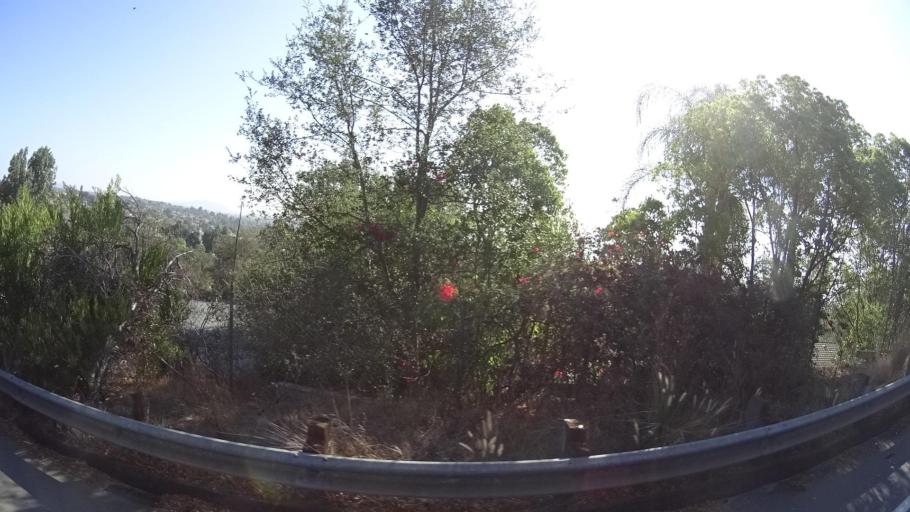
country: US
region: California
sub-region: San Diego County
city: Fallbrook
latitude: 33.3454
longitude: -117.2444
